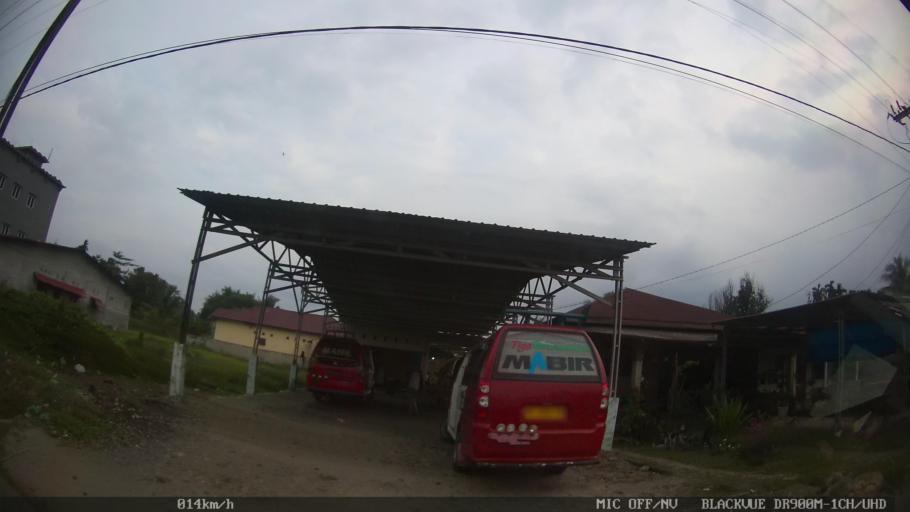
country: ID
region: North Sumatra
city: Sunggal
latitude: 3.5609
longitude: 98.5771
